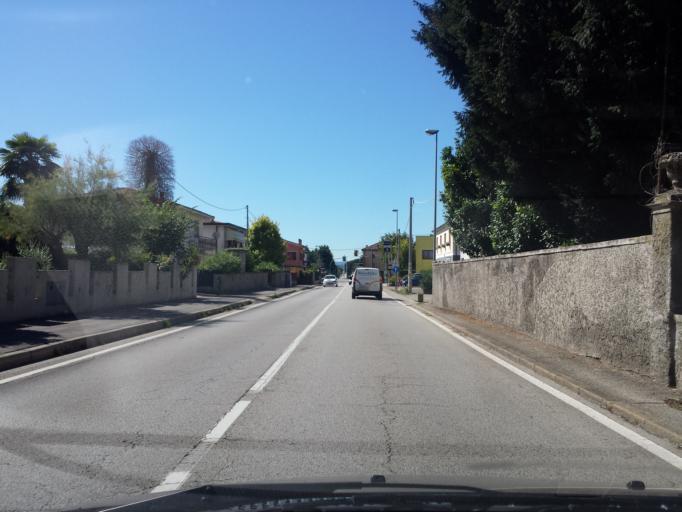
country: IT
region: Veneto
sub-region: Provincia di Vicenza
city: Dueville
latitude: 45.6265
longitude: 11.5703
